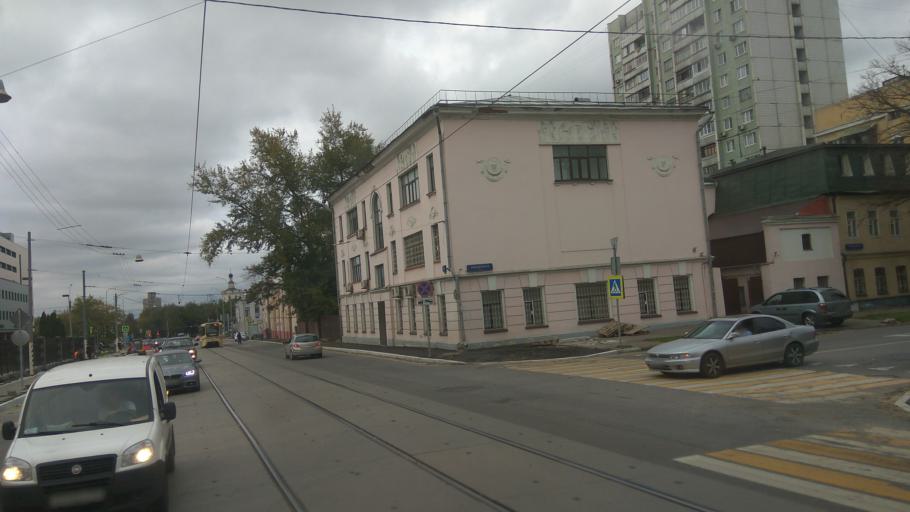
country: RU
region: Moscow
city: Taganskiy
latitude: 55.7443
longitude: 37.6707
